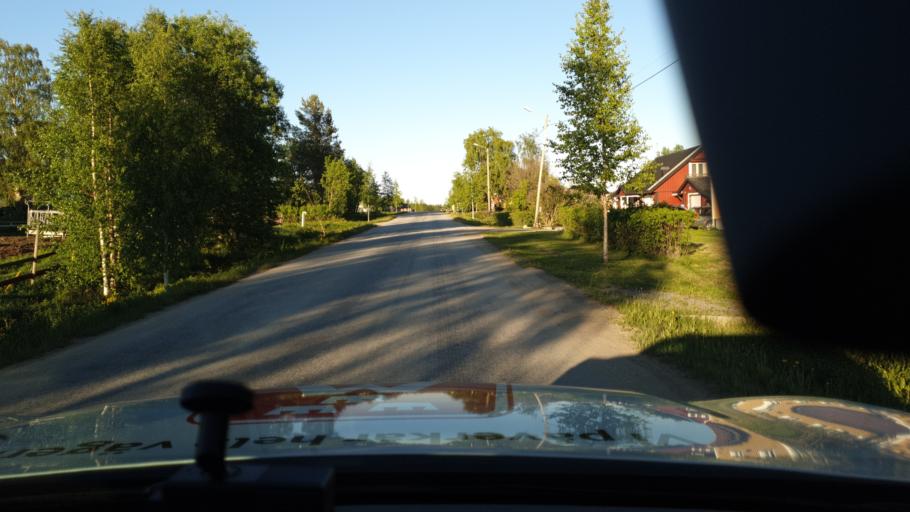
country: SE
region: Vaesterbotten
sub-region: Umea Kommun
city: Roback
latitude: 64.0144
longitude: 20.1247
